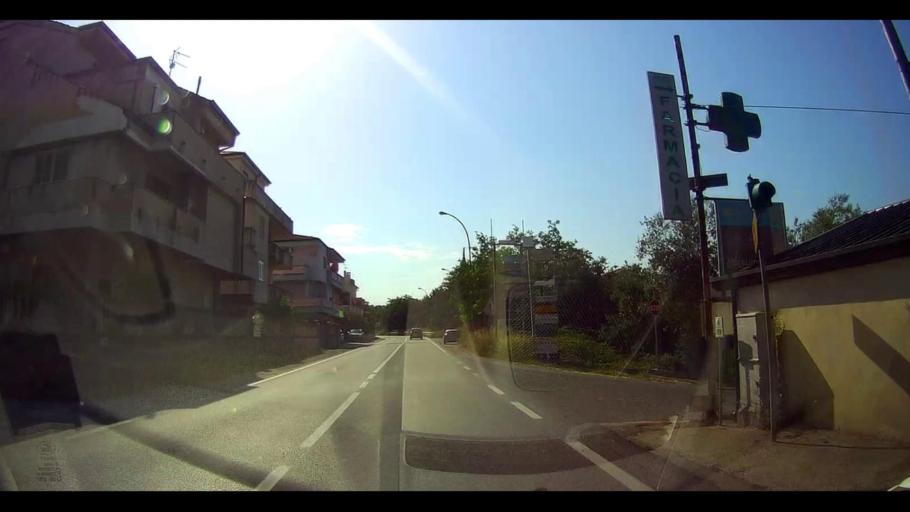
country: IT
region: Calabria
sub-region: Provincia di Cosenza
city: Cariati
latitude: 39.4839
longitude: 16.9739
